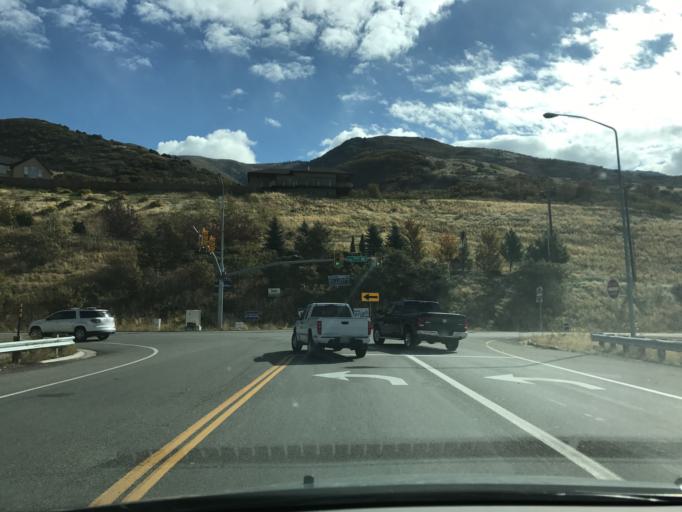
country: US
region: Utah
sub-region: Davis County
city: South Weber
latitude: 41.1076
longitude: -111.9095
